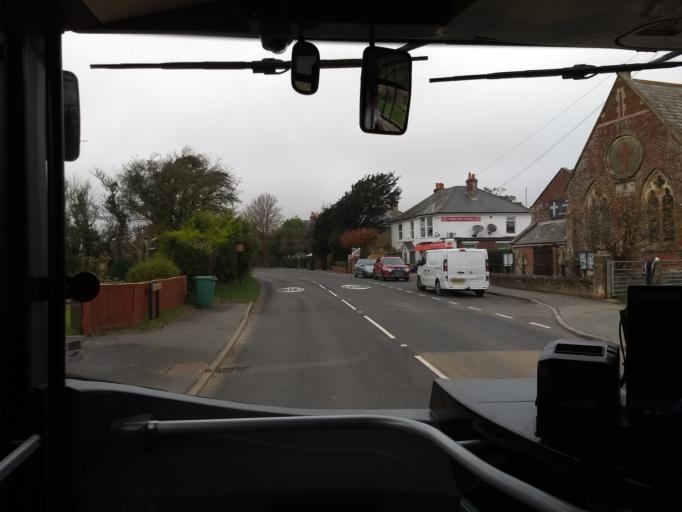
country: GB
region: England
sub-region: Isle of Wight
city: Newchurch
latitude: 50.6710
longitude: -1.2340
